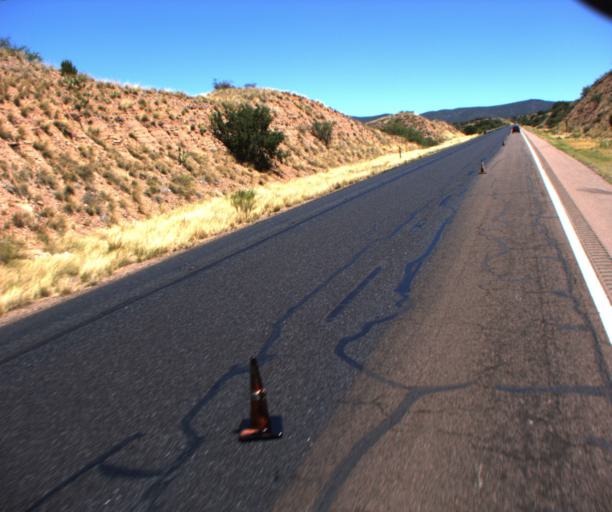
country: US
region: Arizona
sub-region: Gila County
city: Payson
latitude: 34.1144
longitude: -111.3516
